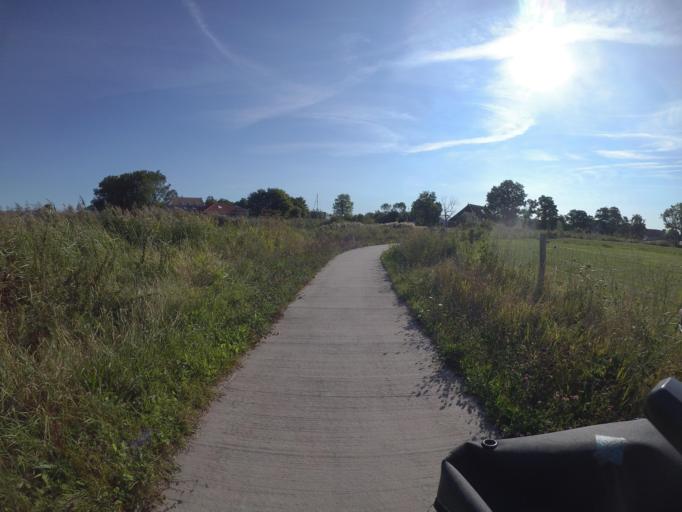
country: NL
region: Friesland
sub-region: Gemeente Dongeradeel
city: Dokkum
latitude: 53.3229
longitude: 5.9787
